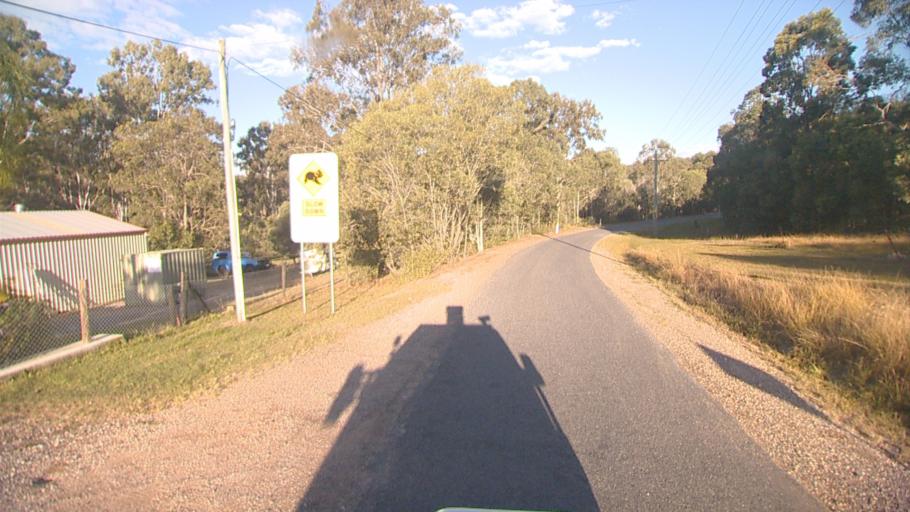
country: AU
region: Queensland
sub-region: Logan
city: Waterford West
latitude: -27.7399
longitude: 153.1478
